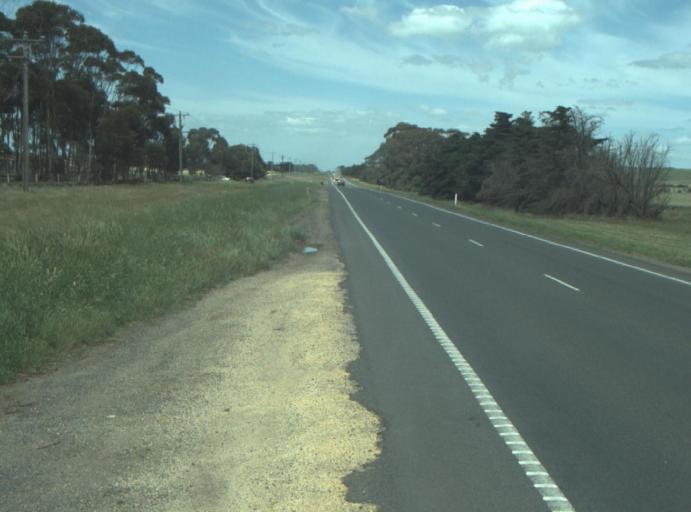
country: AU
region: Victoria
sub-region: Greater Geelong
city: Lara
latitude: -38.0048
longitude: 144.3496
